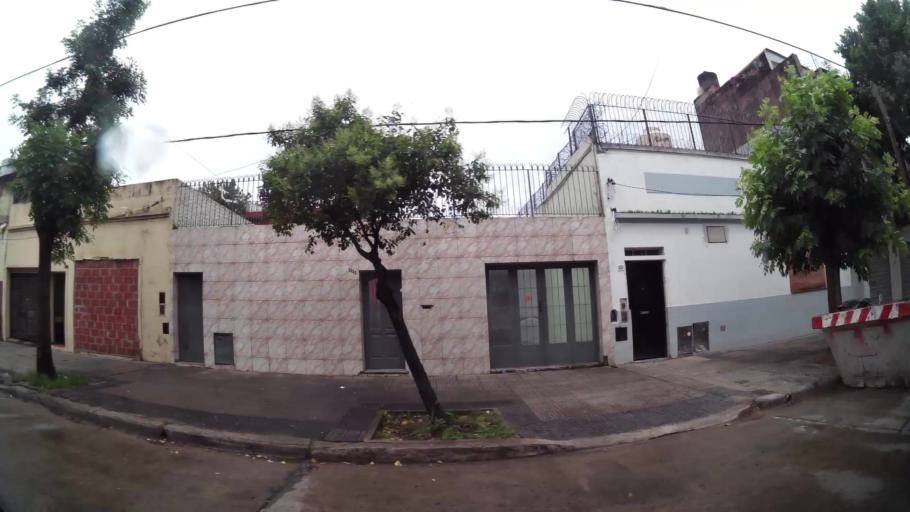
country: AR
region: Buenos Aires F.D.
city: Villa Lugano
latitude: -34.6632
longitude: -58.4391
